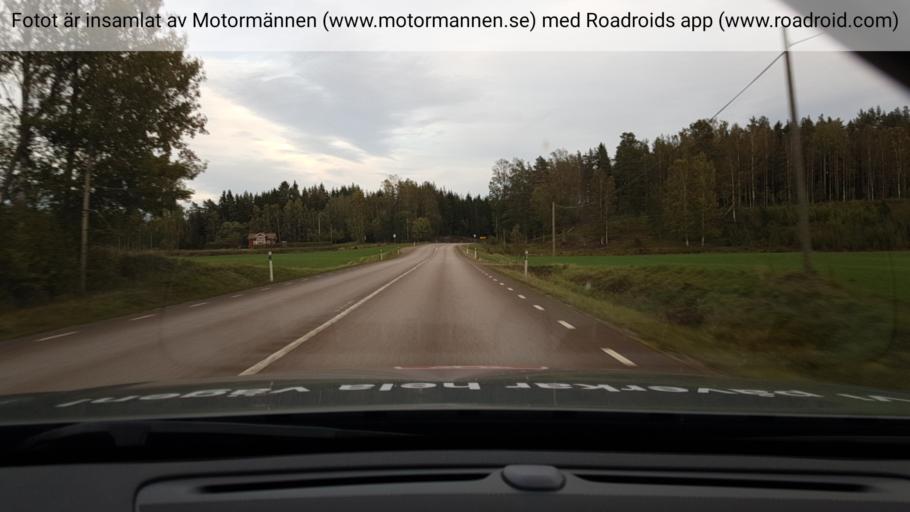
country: SE
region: Vaestra Goetaland
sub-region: Amals Kommun
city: Amal
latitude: 59.0716
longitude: 12.6454
